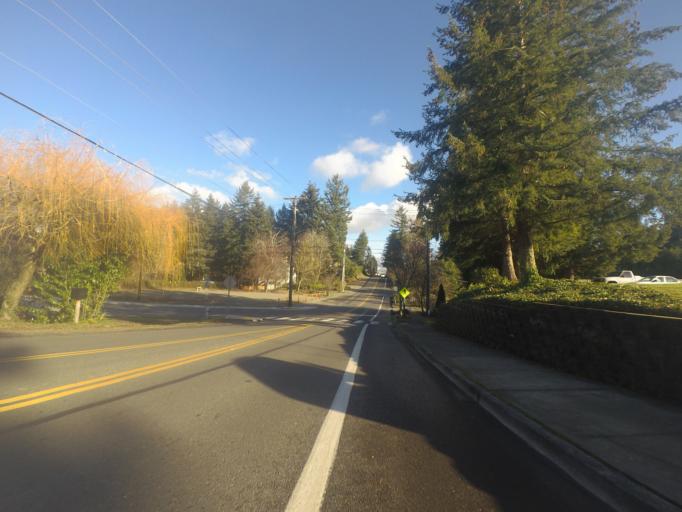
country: US
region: Washington
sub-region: Pierce County
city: University Place
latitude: 47.2280
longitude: -122.5348
